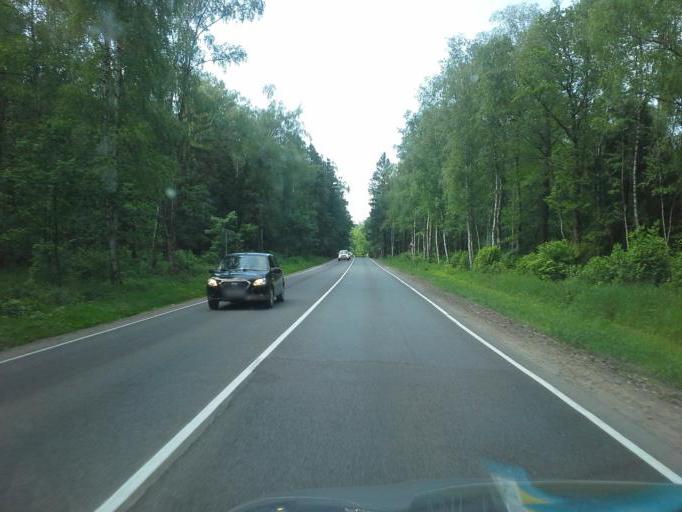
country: RU
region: Moskovskaya
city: Gorki Vtoryye
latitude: 55.7077
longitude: 37.2211
